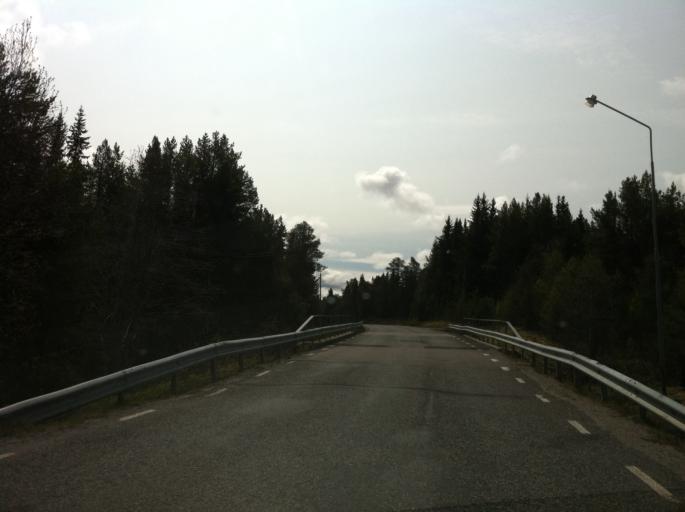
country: NO
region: Hedmark
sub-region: Engerdal
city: Engerdal
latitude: 62.4408
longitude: 12.6795
